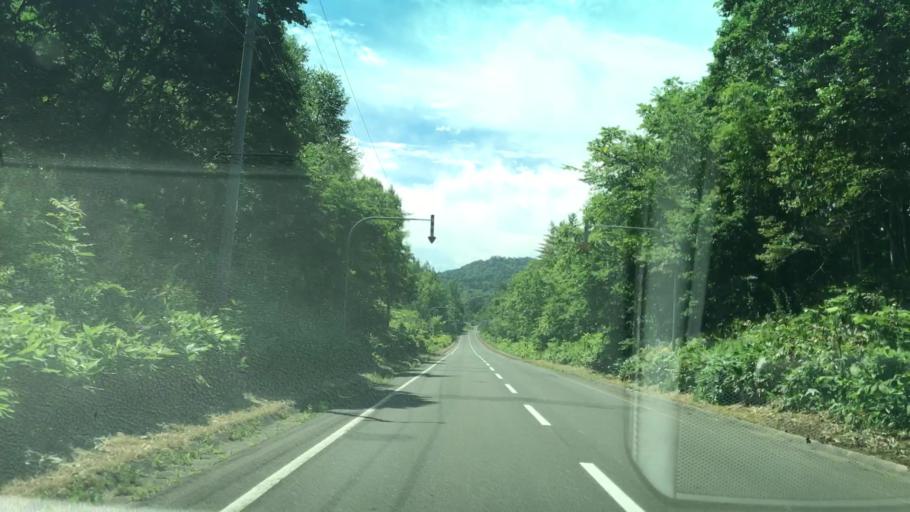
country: JP
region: Hokkaido
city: Shimo-furano
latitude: 42.9651
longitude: 142.4277
